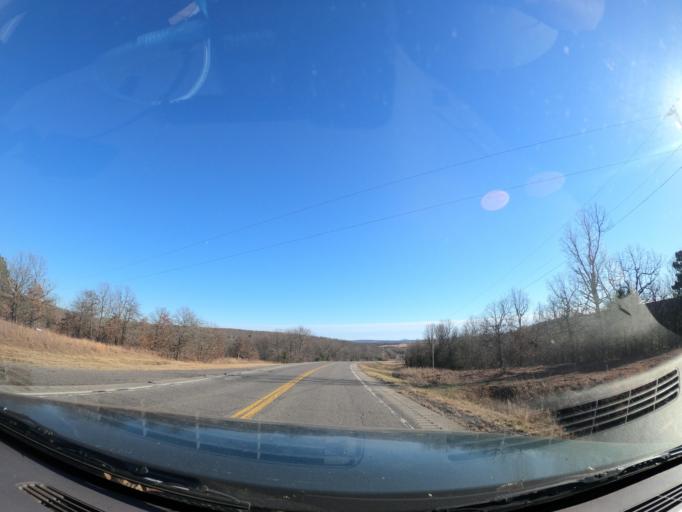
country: US
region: Oklahoma
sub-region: Pittsburg County
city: Longtown
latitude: 35.2230
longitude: -95.4308
